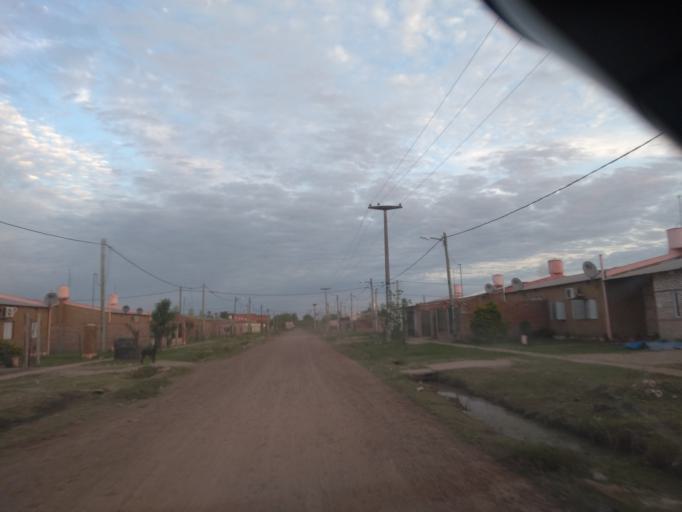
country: AR
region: Chaco
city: Fontana
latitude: -27.4141
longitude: -59.0552
